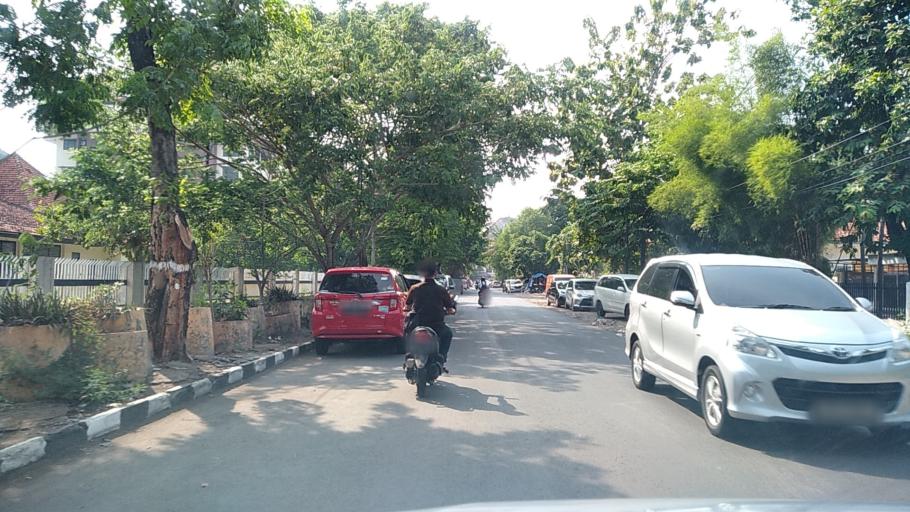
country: ID
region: Central Java
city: Semarang
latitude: -6.9942
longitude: 110.4254
